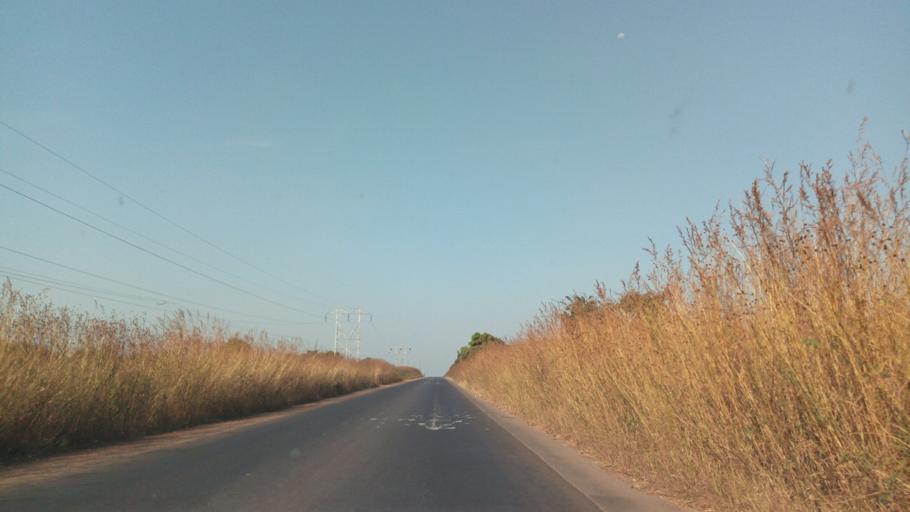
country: CD
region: Katanga
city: Likasi
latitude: -11.0012
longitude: 26.8727
